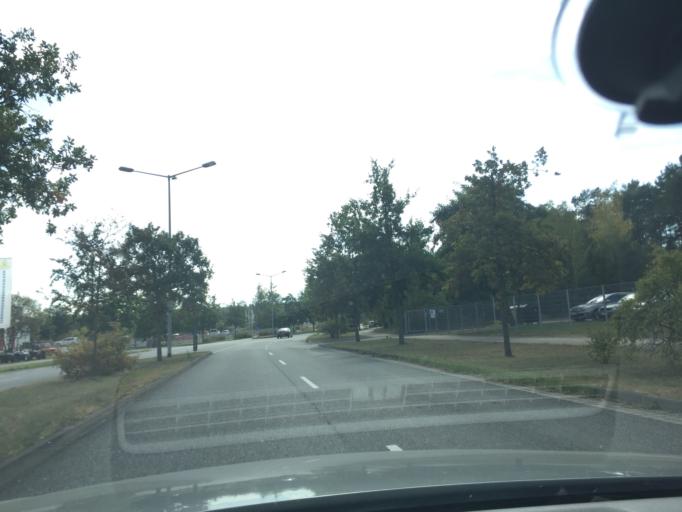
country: DE
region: Brandenburg
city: Grunheide
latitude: 52.3864
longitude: 13.7999
